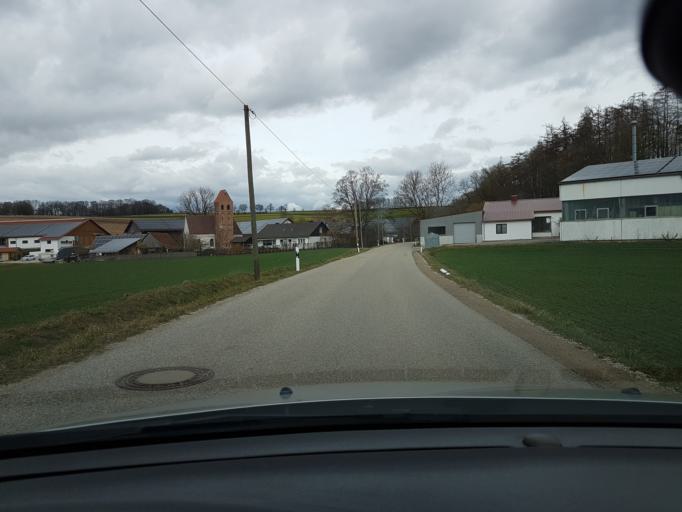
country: DE
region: Bavaria
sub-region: Lower Bavaria
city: Landshut
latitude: 48.5181
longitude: 12.1756
